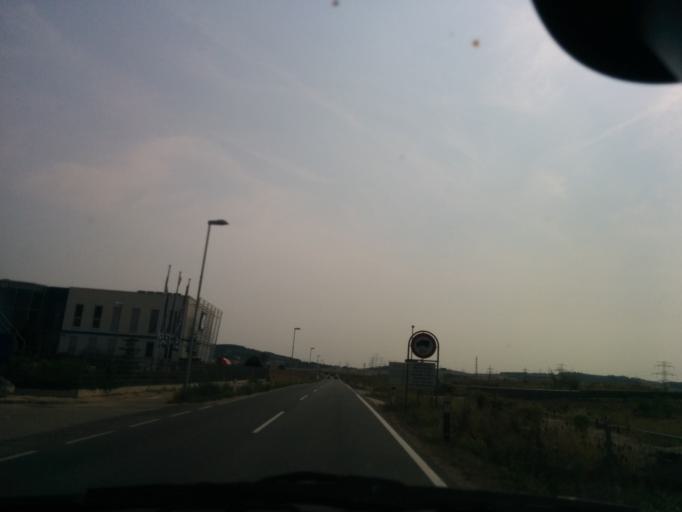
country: AT
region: Lower Austria
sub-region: Politischer Bezirk Korneuburg
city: Harmannsdorf
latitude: 48.3648
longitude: 16.3605
